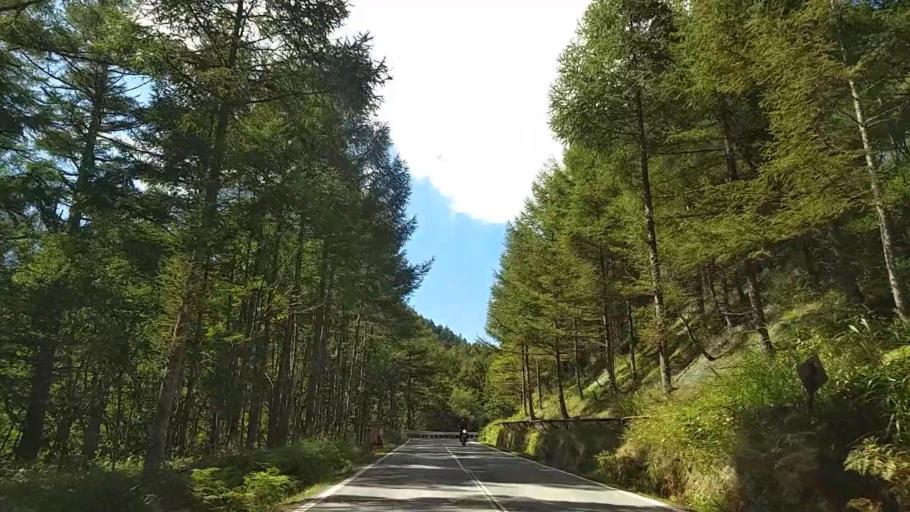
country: JP
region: Nagano
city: Chino
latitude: 36.0831
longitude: 138.2822
